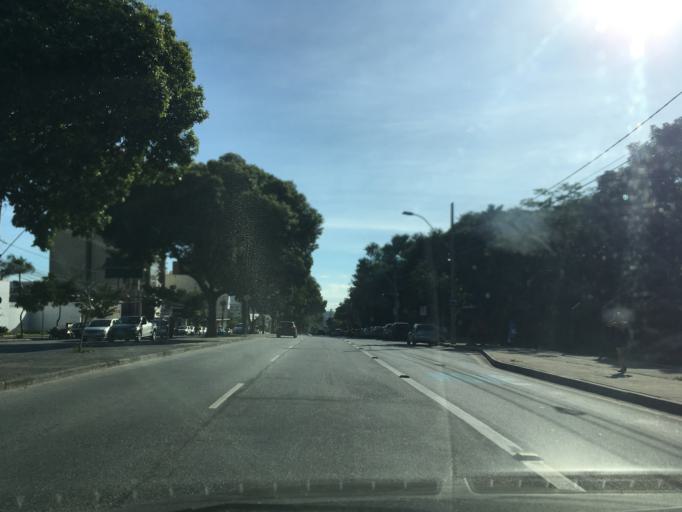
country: BR
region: Minas Gerais
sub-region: Belo Horizonte
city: Belo Horizonte
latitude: -19.8630
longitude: -43.9701
